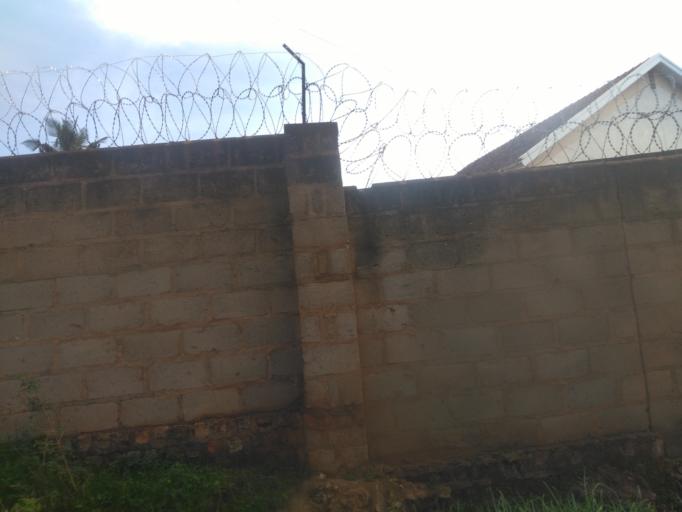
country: UG
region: Central Region
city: Kampala Central Division
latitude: 0.3475
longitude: 32.5952
